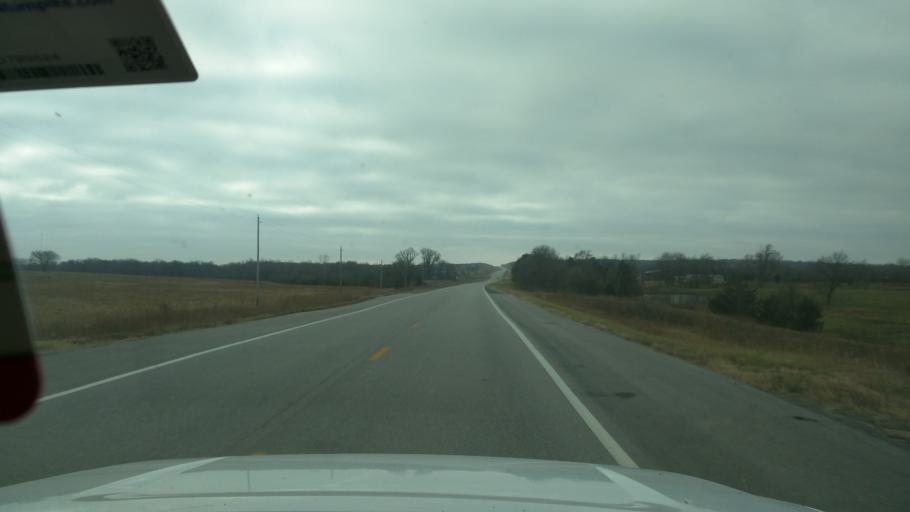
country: US
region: Kansas
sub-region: Elk County
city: Howard
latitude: 37.6259
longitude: -96.2530
